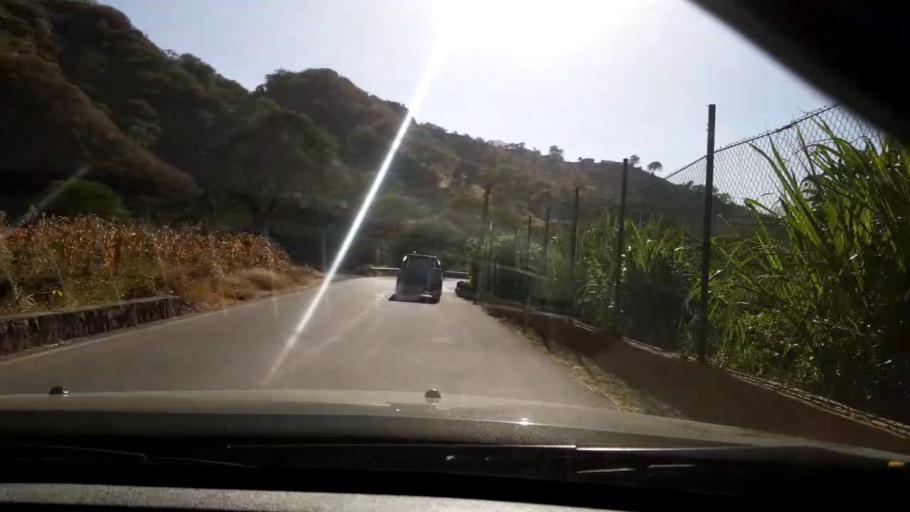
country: CV
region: Sao Lourenco dos Orgaos
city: Joao Teves
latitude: 15.0693
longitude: -23.5740
